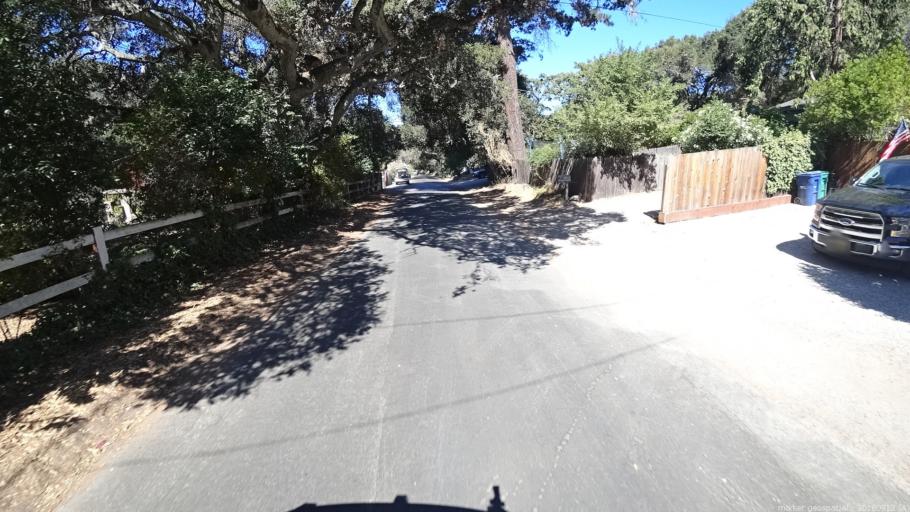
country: US
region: California
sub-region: Monterey County
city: Carmel Valley Village
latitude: 36.4779
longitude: -121.7352
